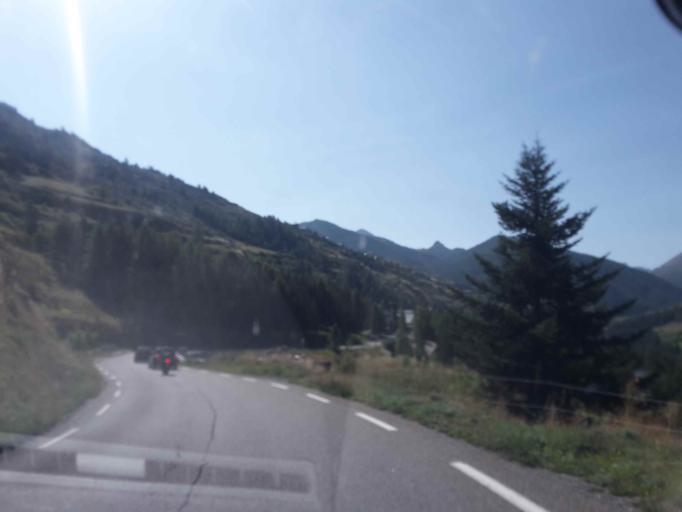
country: FR
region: Provence-Alpes-Cote d'Azur
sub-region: Departement des Hautes-Alpes
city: Guillestre
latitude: 44.6139
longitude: 6.6860
